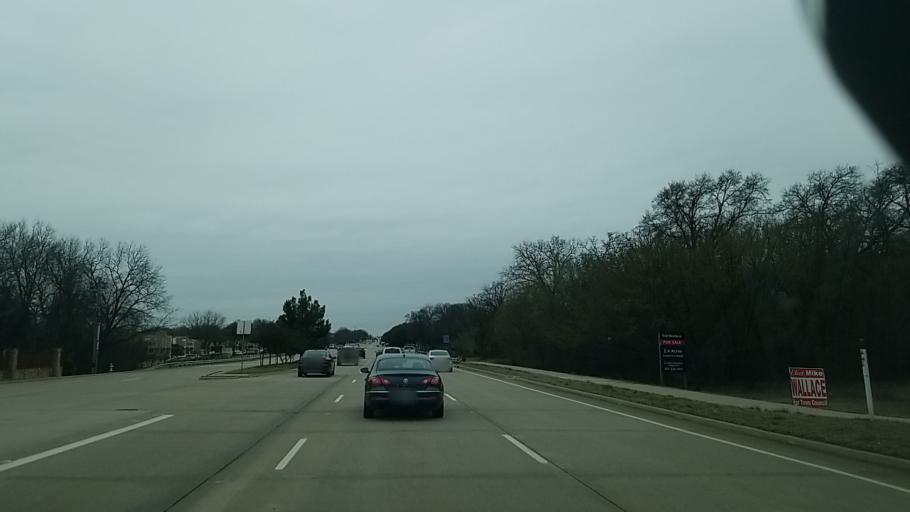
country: US
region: Texas
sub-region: Denton County
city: Flower Mound
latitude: 33.0238
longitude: -97.0709
